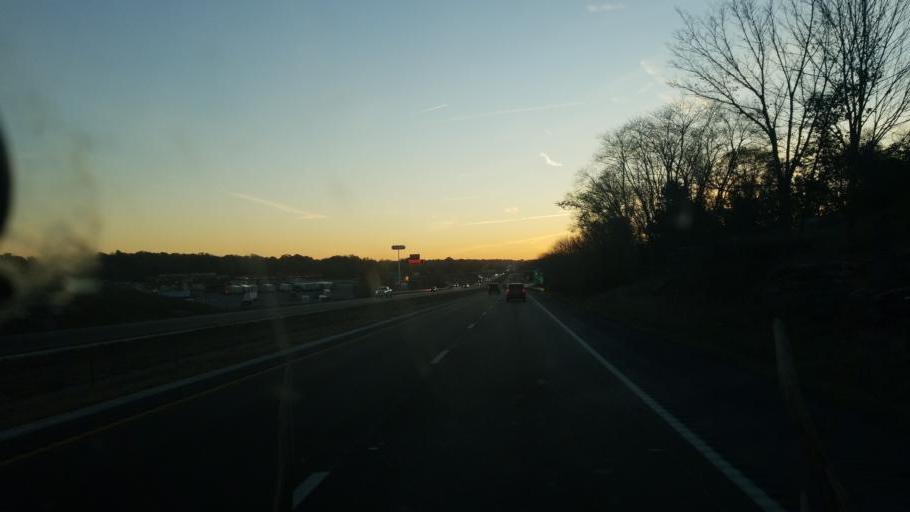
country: US
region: Missouri
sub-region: Boone County
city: Columbia
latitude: 38.9718
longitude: -92.4384
